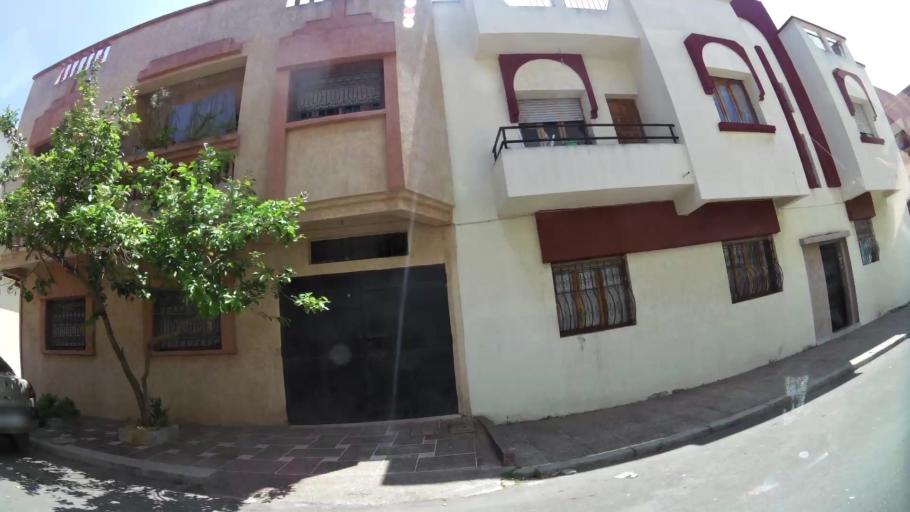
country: MA
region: Gharb-Chrarda-Beni Hssen
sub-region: Kenitra Province
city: Kenitra
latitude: 34.2684
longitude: -6.6136
